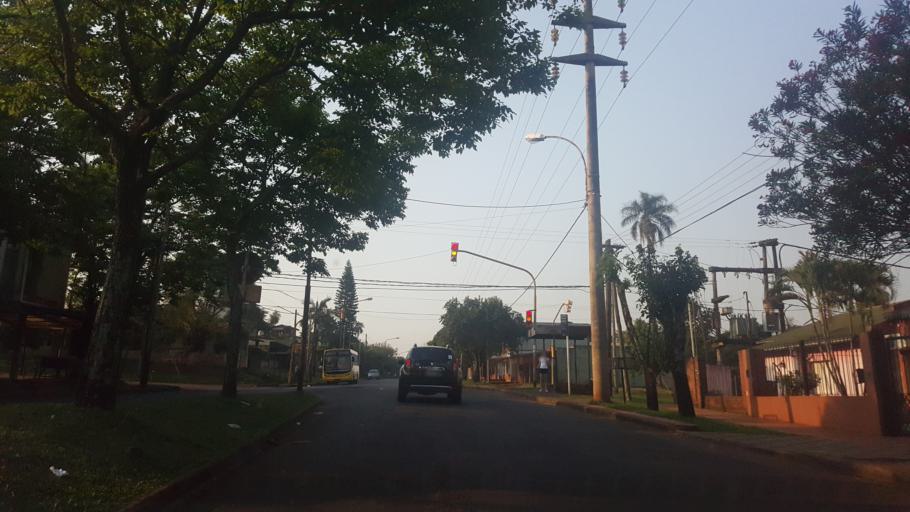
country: AR
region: Misiones
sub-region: Departamento de Capital
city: Posadas
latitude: -27.3889
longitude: -55.8930
